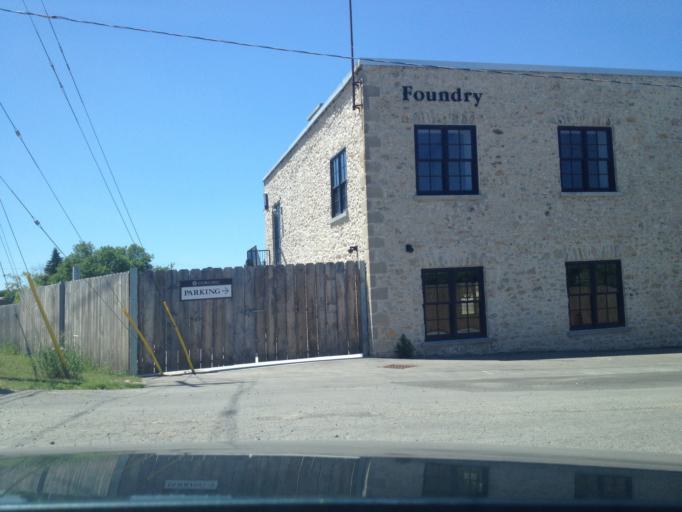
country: CA
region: Ontario
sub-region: Wellington County
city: Guelph
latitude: 43.6798
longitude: -80.4302
